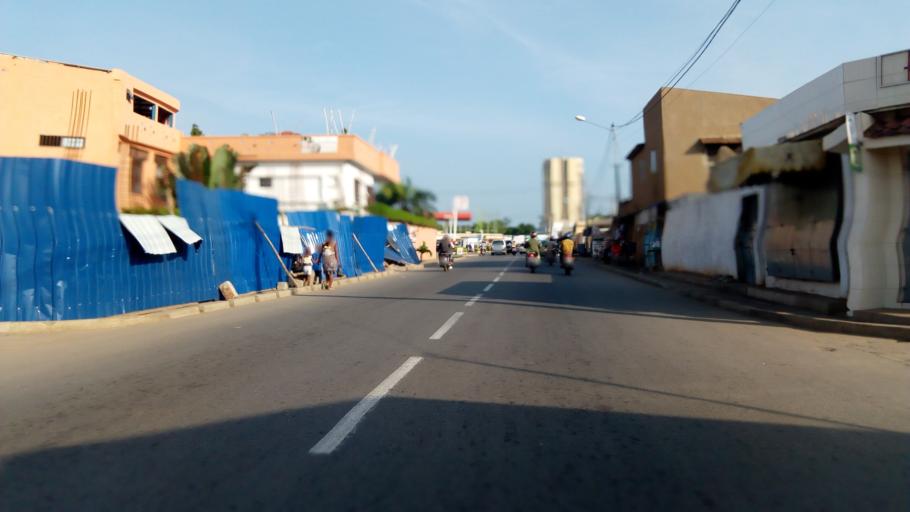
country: TG
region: Maritime
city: Lome
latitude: 6.1320
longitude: 1.2118
